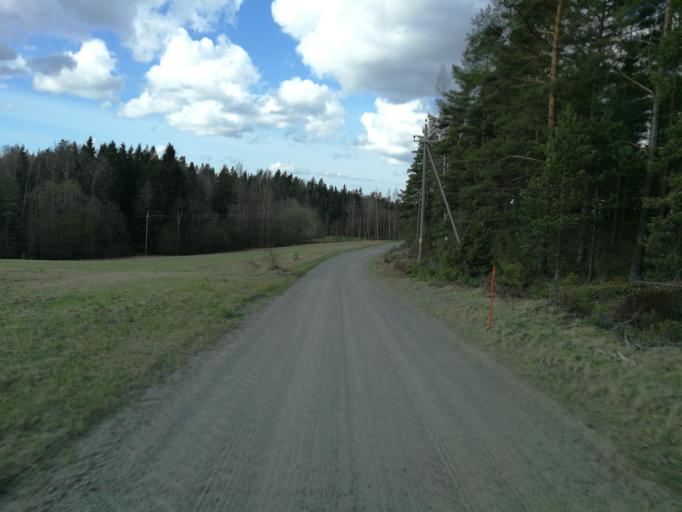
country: FI
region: Uusimaa
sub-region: Raaseporin
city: Inga
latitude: 60.0988
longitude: 23.9447
